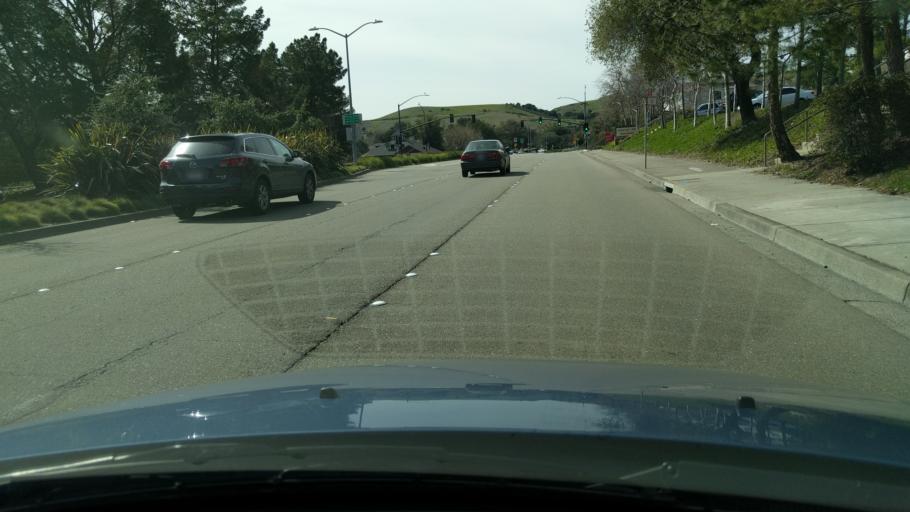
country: US
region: California
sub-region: Contra Costa County
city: San Ramon
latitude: 37.7733
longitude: -121.9894
